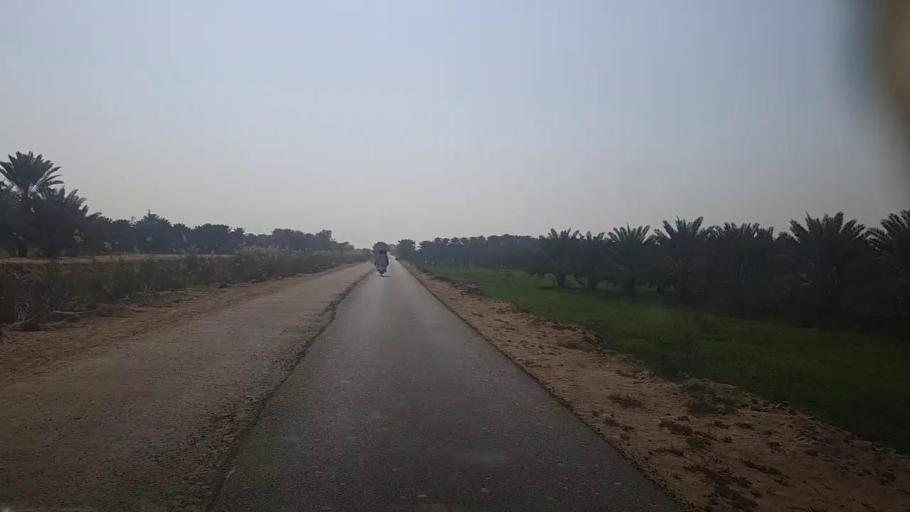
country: PK
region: Sindh
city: Khairpur
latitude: 27.4653
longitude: 68.8180
